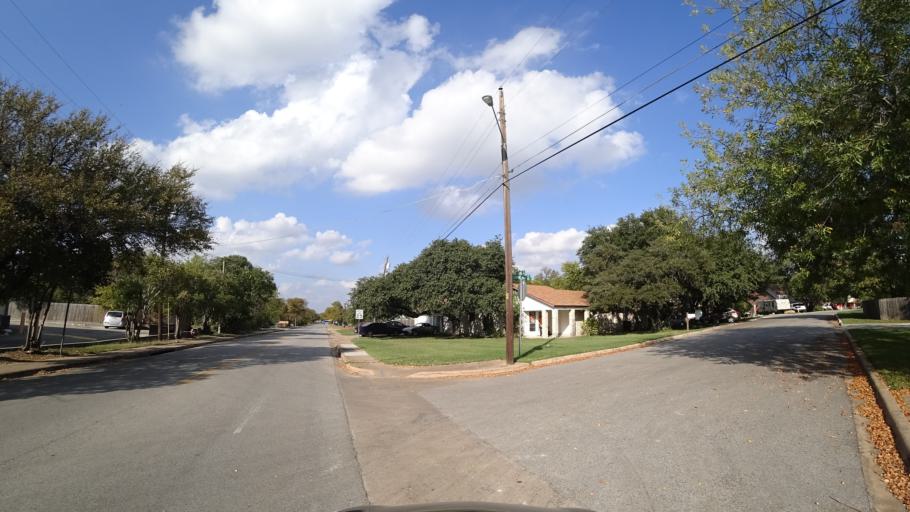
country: US
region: Texas
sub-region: Williamson County
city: Round Rock
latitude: 30.4954
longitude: -97.6750
